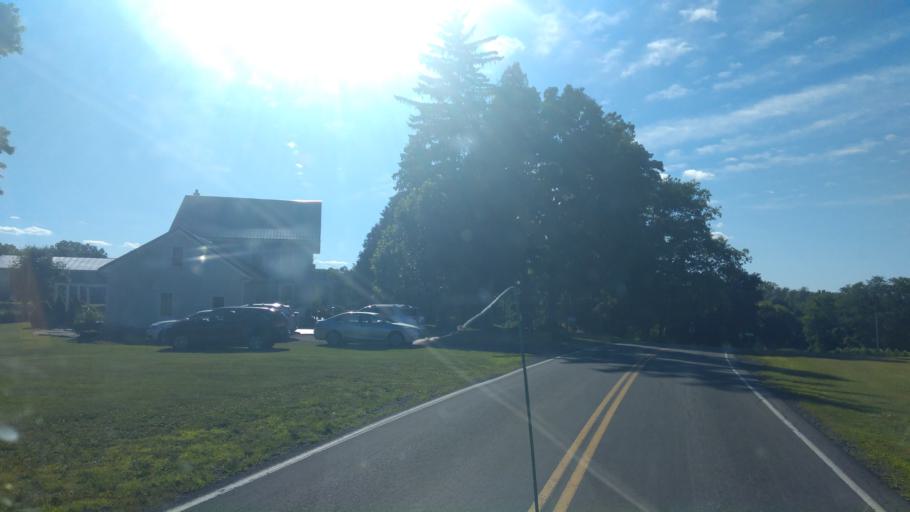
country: US
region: New York
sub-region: Wayne County
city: Lyons
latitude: 43.0026
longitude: -76.9626
